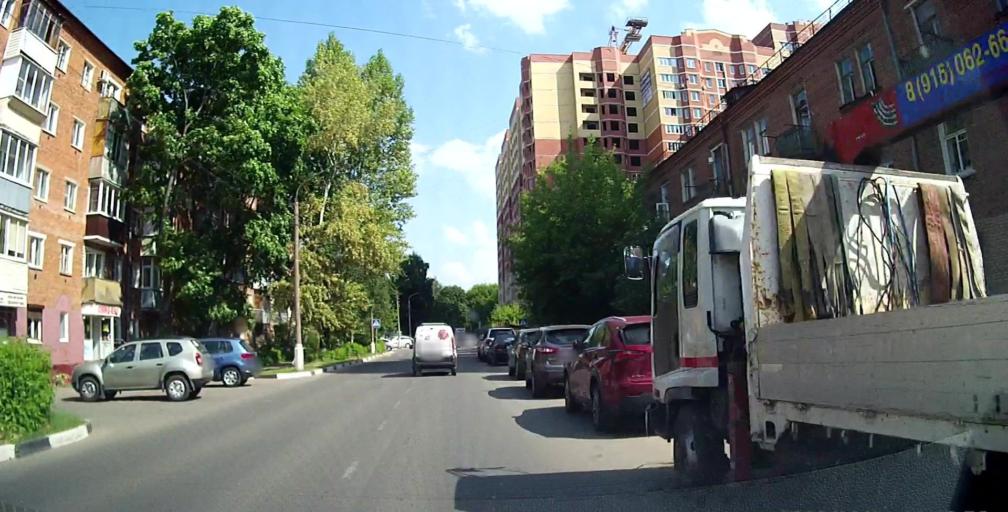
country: RU
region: Moskovskaya
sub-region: Podol'skiy Rayon
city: Podol'sk
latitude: 55.4139
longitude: 37.5358
